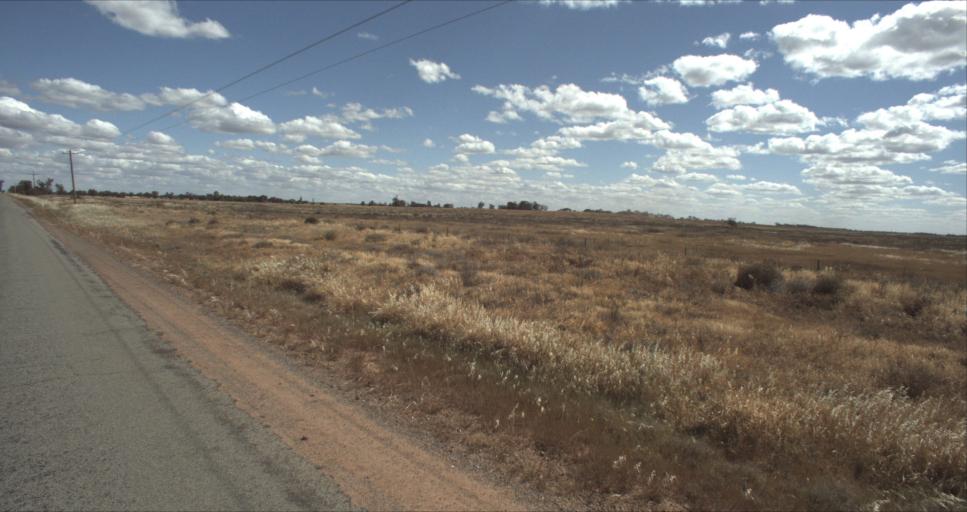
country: AU
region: New South Wales
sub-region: Leeton
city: Leeton
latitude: -34.4767
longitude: 146.2499
